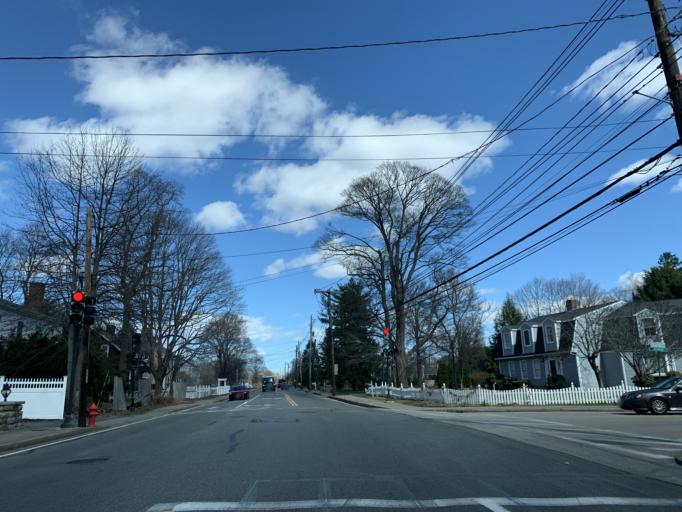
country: US
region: Massachusetts
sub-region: Norfolk County
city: Canton
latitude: 42.1736
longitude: -71.1363
